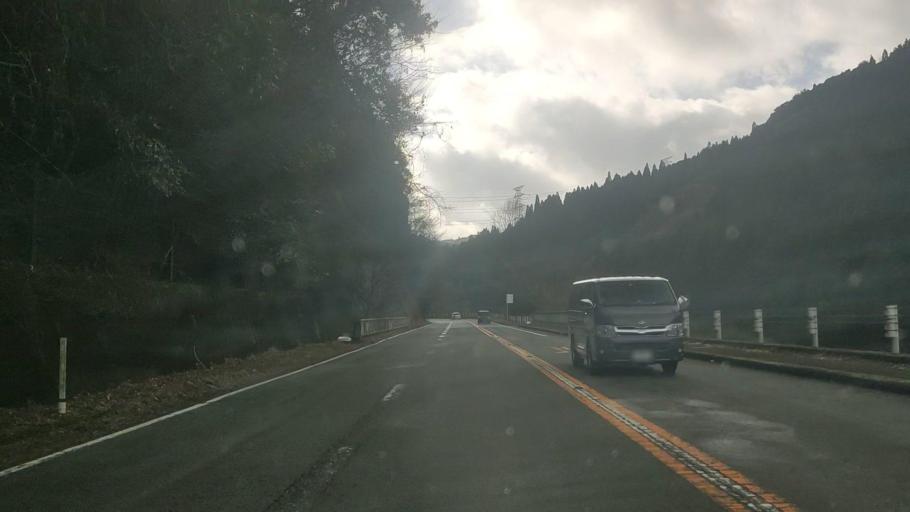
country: JP
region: Kumamoto
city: Hitoyoshi
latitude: 32.1147
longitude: 130.8061
